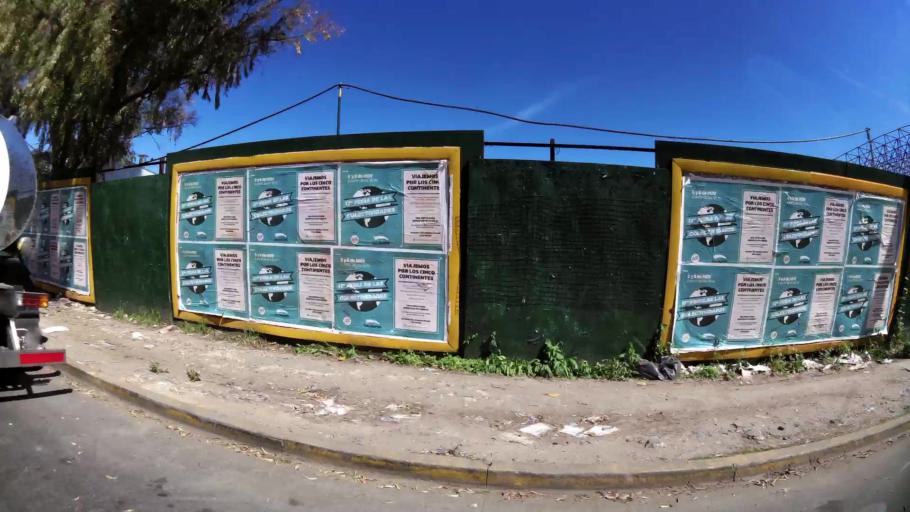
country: AR
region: Buenos Aires
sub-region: Partido de General San Martin
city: General San Martin
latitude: -34.5600
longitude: -58.5263
